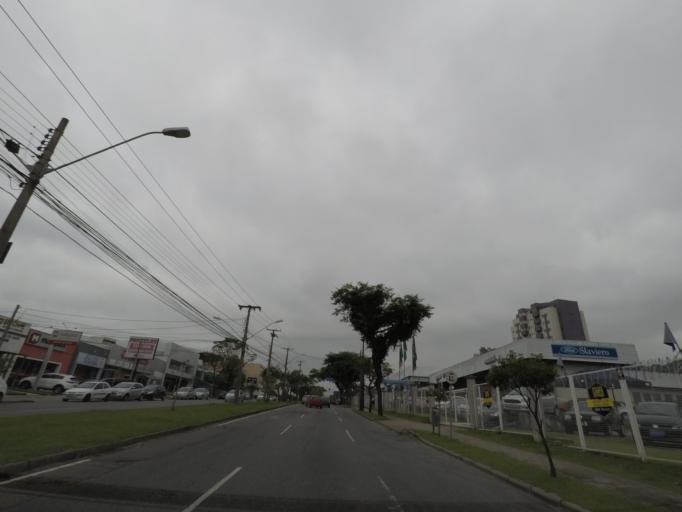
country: BR
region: Parana
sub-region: Curitiba
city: Curitiba
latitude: -25.4753
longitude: -49.2896
